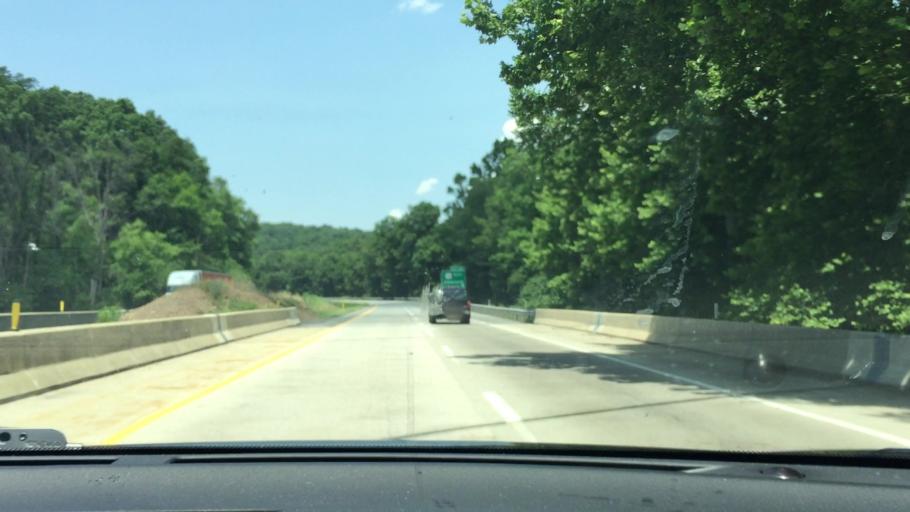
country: US
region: Maryland
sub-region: Washington County
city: Hancock
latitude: 39.7889
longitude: -78.2113
